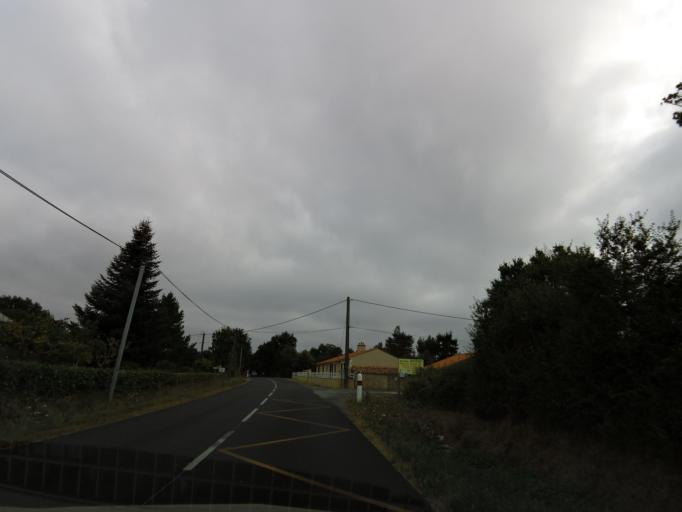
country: FR
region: Pays de la Loire
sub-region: Departement de la Vendee
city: Avrille
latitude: 46.4653
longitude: -1.4522
